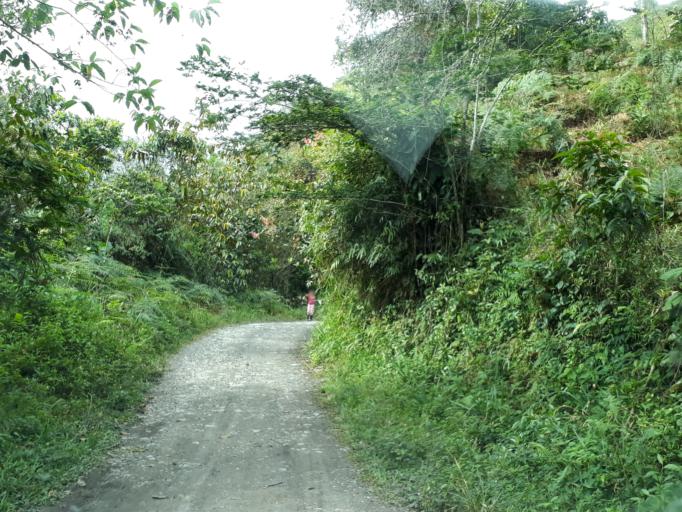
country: CO
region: Boyaca
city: Quipama
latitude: 5.3943
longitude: -74.1282
